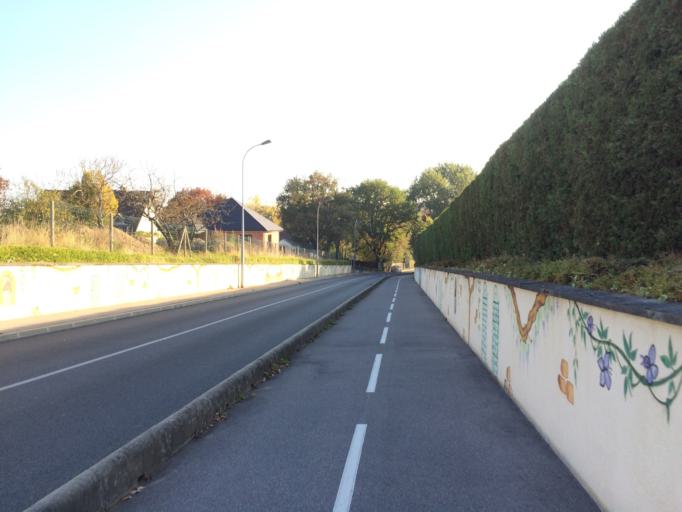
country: FR
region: Ile-de-France
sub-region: Departement de l'Essonne
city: Villejust
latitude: 48.6753
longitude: 2.2390
